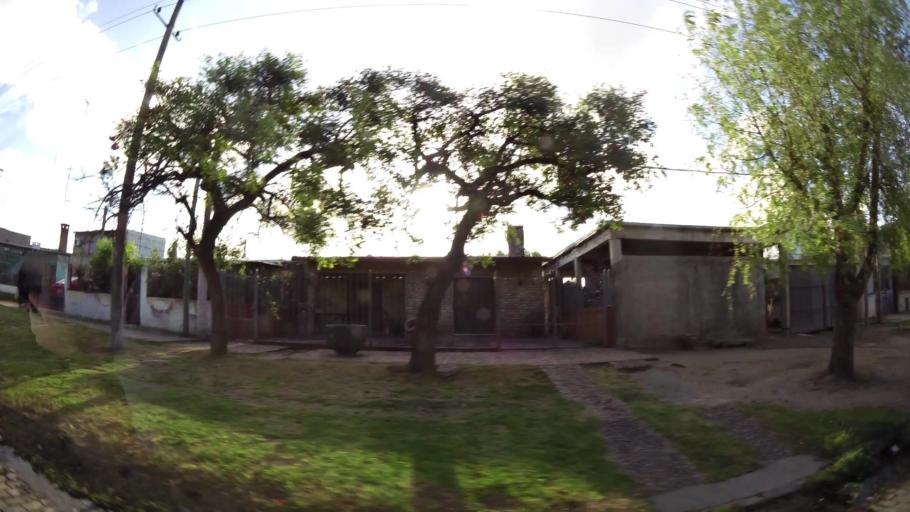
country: UY
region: Montevideo
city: Montevideo
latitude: -34.8829
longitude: -56.2650
